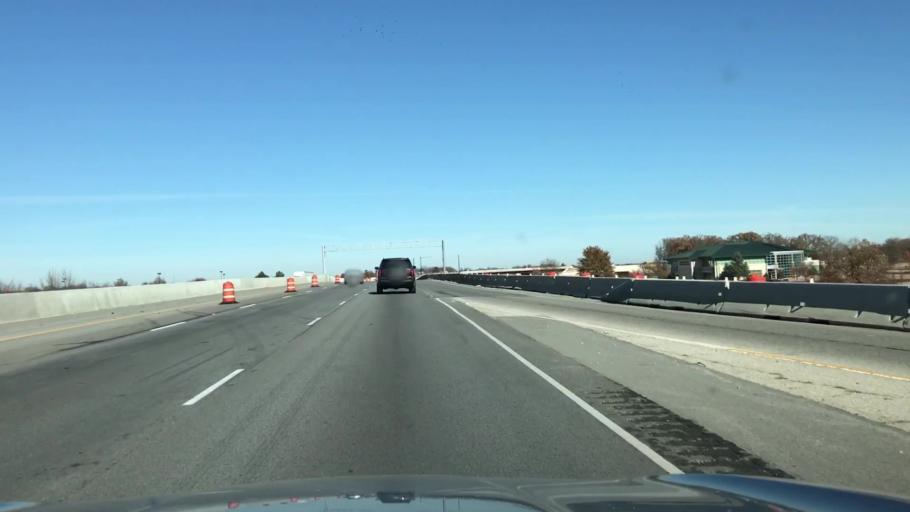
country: US
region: Arkansas
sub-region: Benton County
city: Bentonville
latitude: 36.3591
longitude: -94.1775
